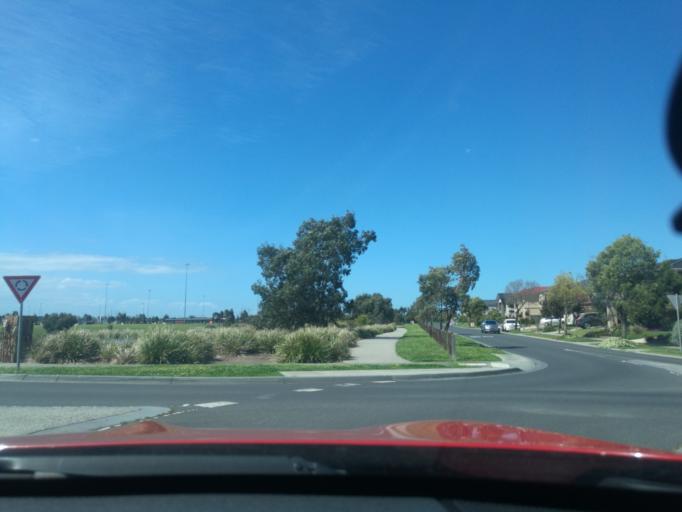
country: AU
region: Victoria
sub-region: Casey
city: Lynbrook
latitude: -38.0738
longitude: 145.2458
